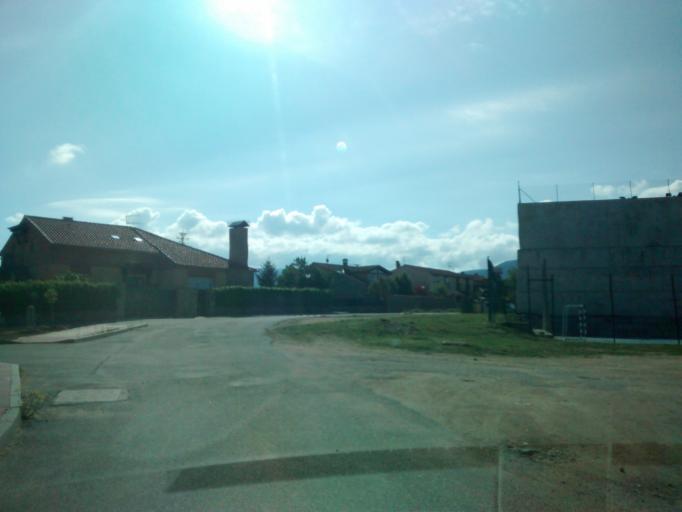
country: ES
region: Castille and Leon
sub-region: Provincia de Segovia
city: Torrecaballeros
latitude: 40.9957
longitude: -4.0195
